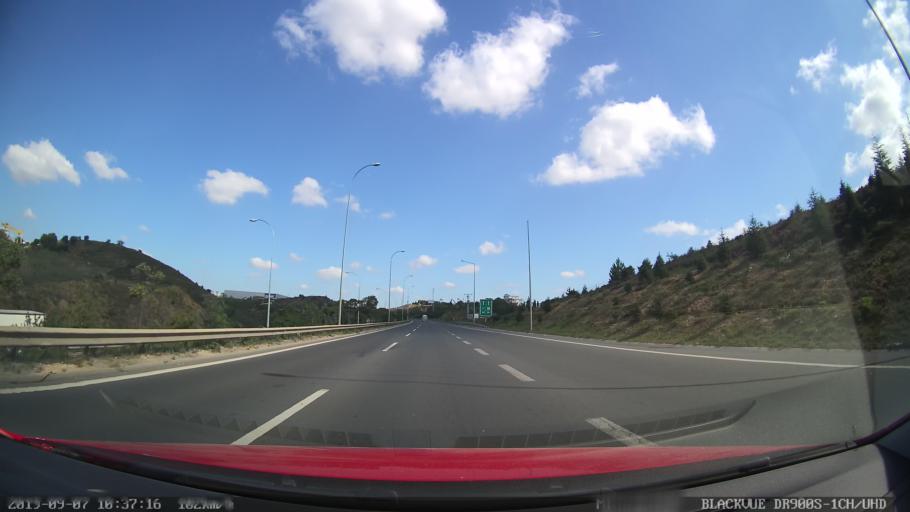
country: TR
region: Kocaeli
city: Balcik
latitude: 40.8440
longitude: 29.3745
